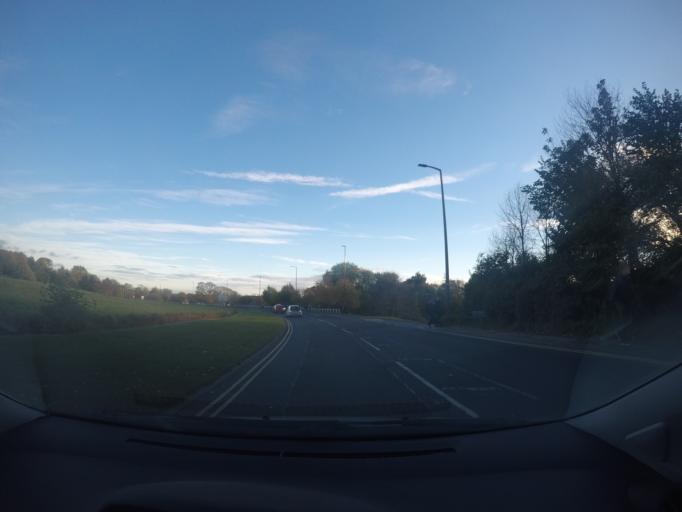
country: GB
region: England
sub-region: City of York
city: Heslington
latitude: 53.9507
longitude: -1.0592
